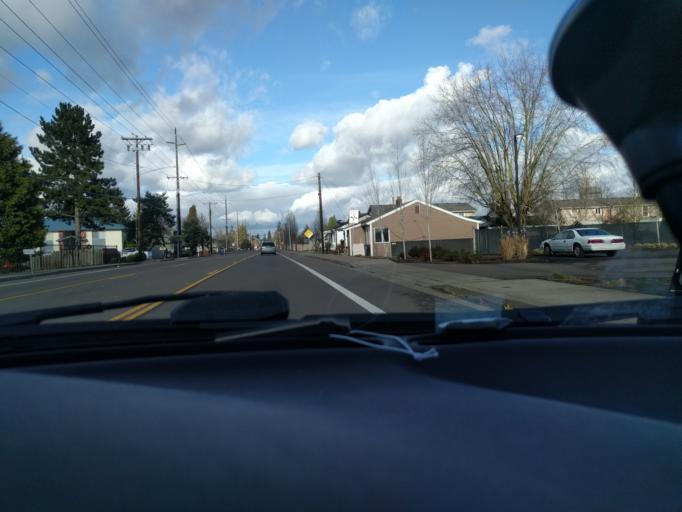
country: US
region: Oregon
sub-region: Marion County
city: Hayesville
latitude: 44.9689
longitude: -122.9917
